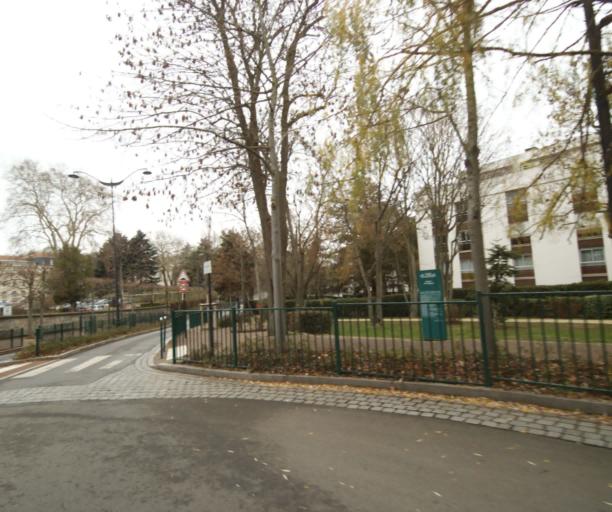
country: FR
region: Ile-de-France
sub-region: Departement des Hauts-de-Seine
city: Garches
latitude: 48.8594
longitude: 2.1832
